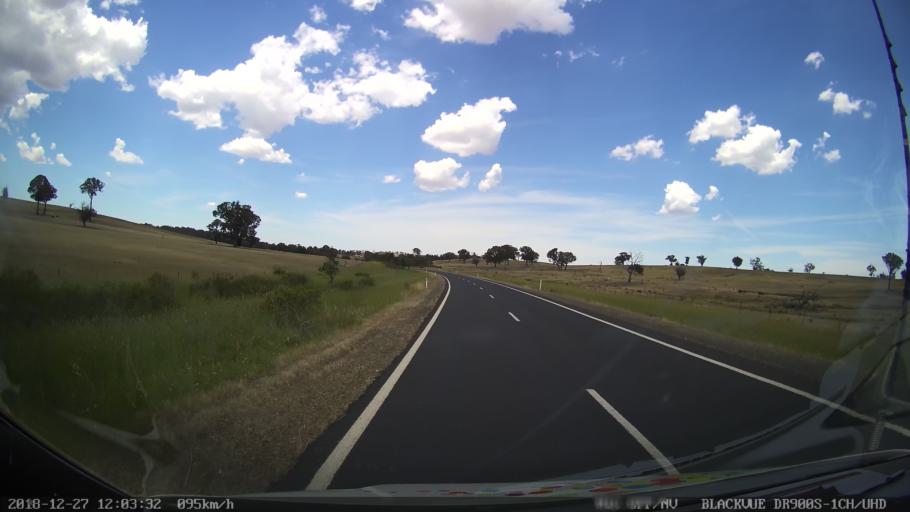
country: AU
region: New South Wales
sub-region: Blayney
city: Blayney
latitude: -33.7865
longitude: 149.3580
